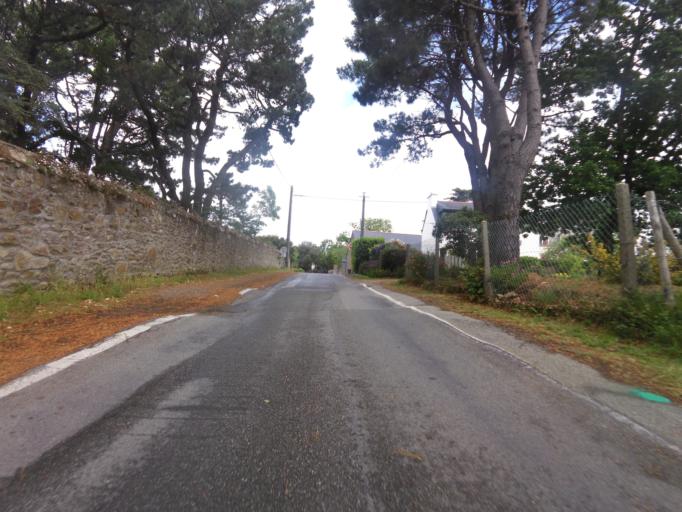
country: FR
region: Brittany
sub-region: Departement du Morbihan
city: Larmor-Baden
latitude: 47.5865
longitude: -2.8930
